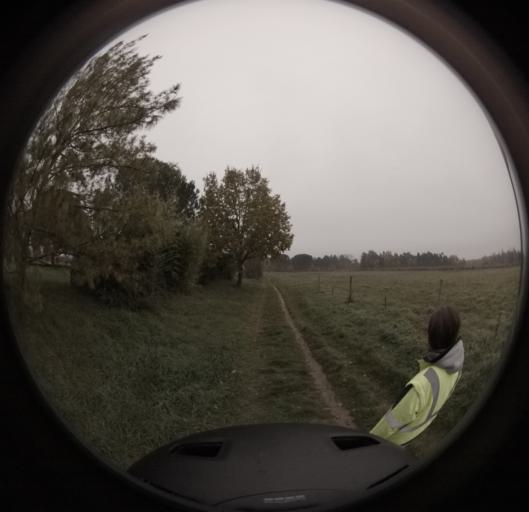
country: FR
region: Midi-Pyrenees
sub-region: Departement du Tarn-et-Garonne
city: Saint-Nauphary
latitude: 43.9999
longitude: 1.3980
